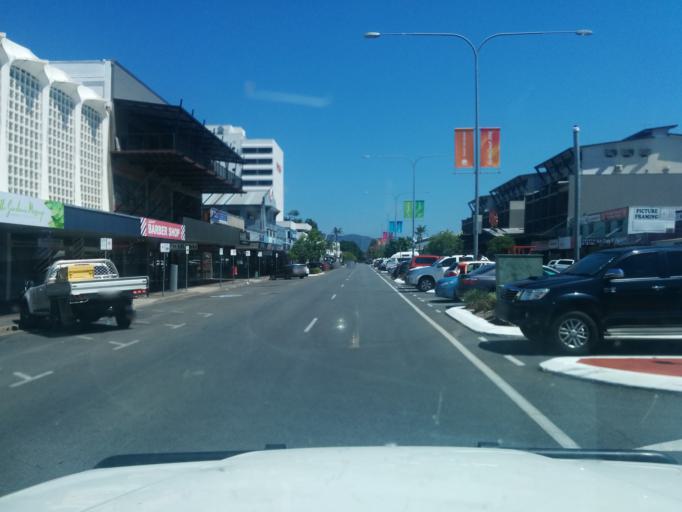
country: AU
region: Queensland
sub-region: Cairns
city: Cairns
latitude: -16.9231
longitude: 145.7750
